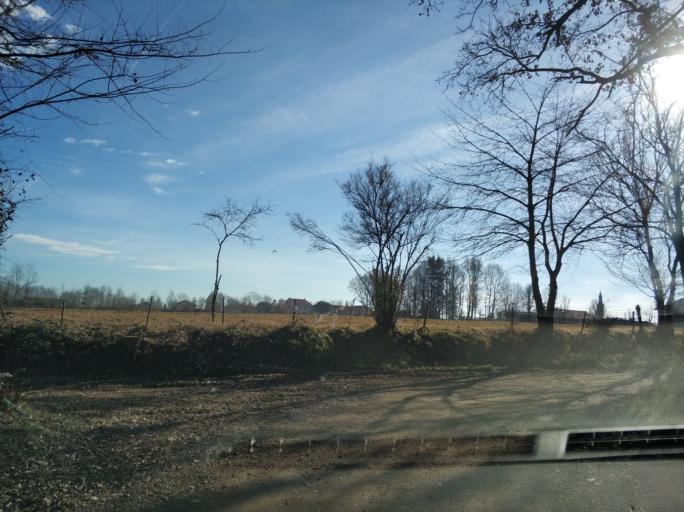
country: IT
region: Piedmont
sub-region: Provincia di Torino
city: San Carlo Canavese
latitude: 45.2536
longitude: 7.6074
